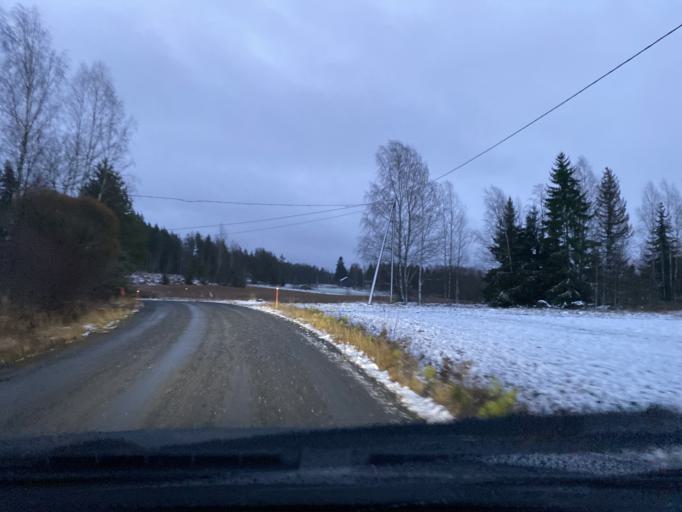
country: FI
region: Pirkanmaa
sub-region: Lounais-Pirkanmaa
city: Punkalaidun
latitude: 61.1628
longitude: 22.9552
